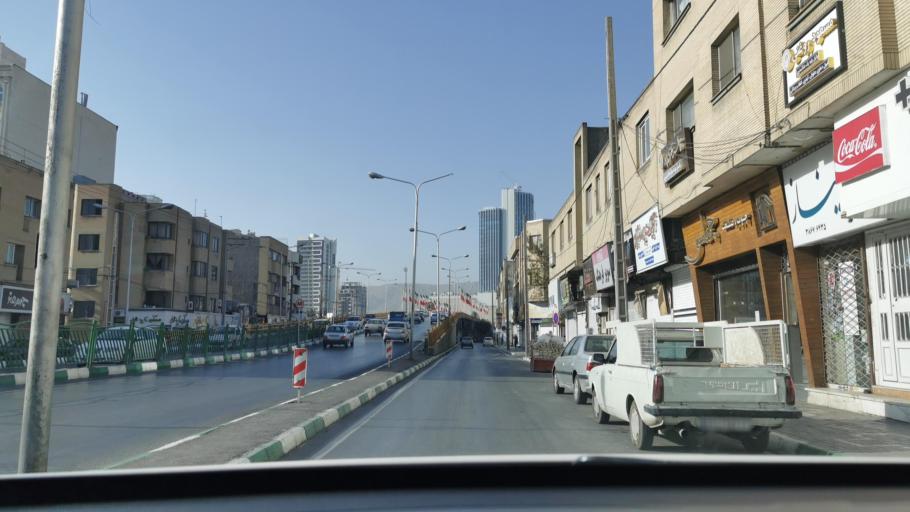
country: IR
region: Razavi Khorasan
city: Mashhad
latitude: 36.3296
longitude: 59.5024
